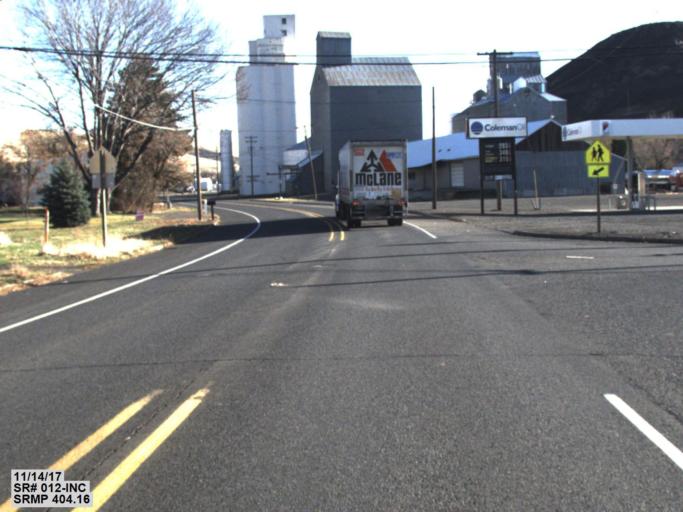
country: US
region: Washington
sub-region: Garfield County
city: Pomeroy
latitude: 46.4740
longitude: -117.5859
